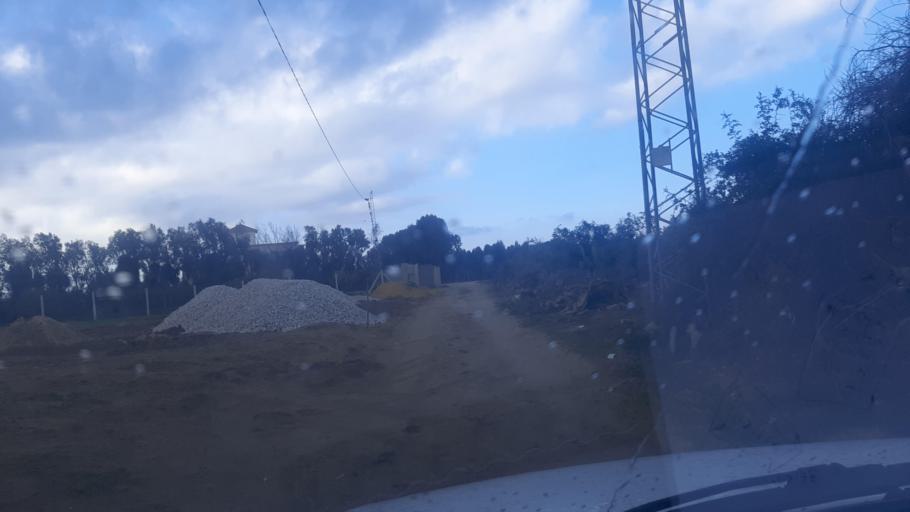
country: TN
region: Nabul
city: Qurbus
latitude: 36.7445
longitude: 10.5262
